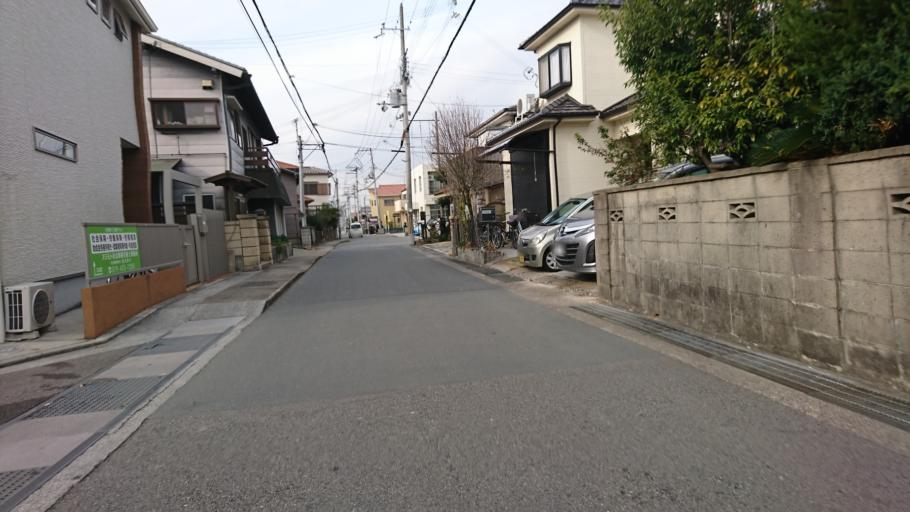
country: JP
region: Hyogo
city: Kakogawacho-honmachi
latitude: 34.7672
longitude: 134.8544
